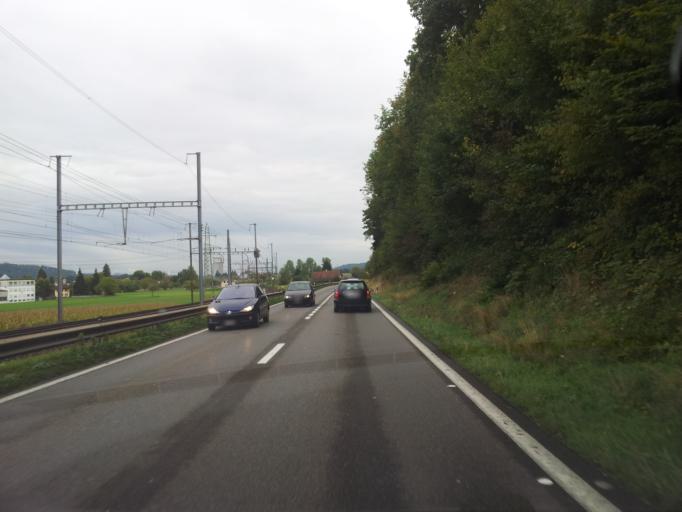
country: CH
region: Aargau
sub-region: Bezirk Lenzburg
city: Othmarsingen
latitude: 47.3869
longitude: 8.2105
